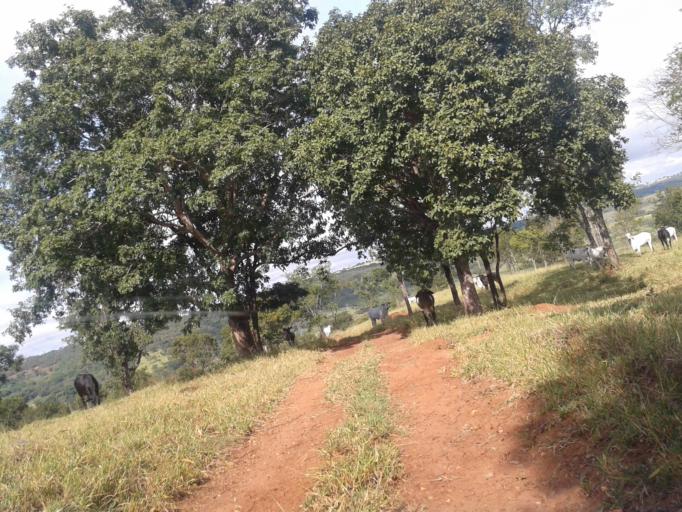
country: BR
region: Minas Gerais
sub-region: Campina Verde
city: Campina Verde
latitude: -19.4256
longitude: -49.6565
